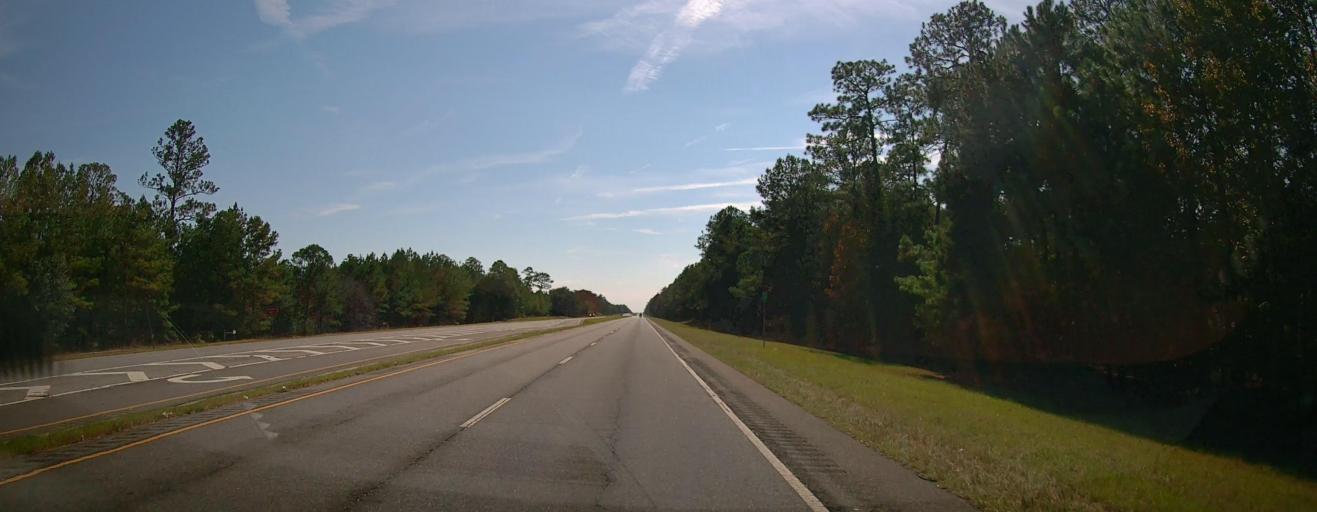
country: US
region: Georgia
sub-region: Lee County
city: Leesburg
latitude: 31.7070
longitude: -83.9904
